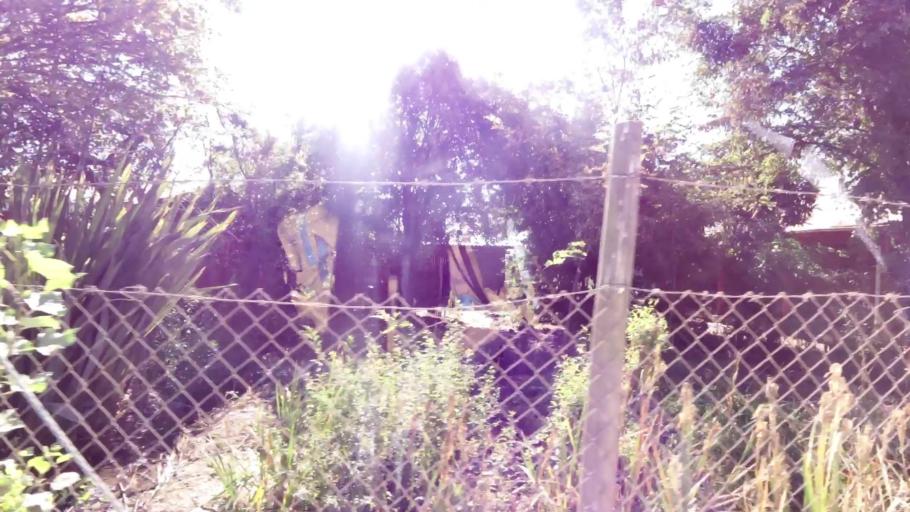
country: CL
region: Maule
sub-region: Provincia de Talca
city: Talca
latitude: -35.4187
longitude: -71.6032
